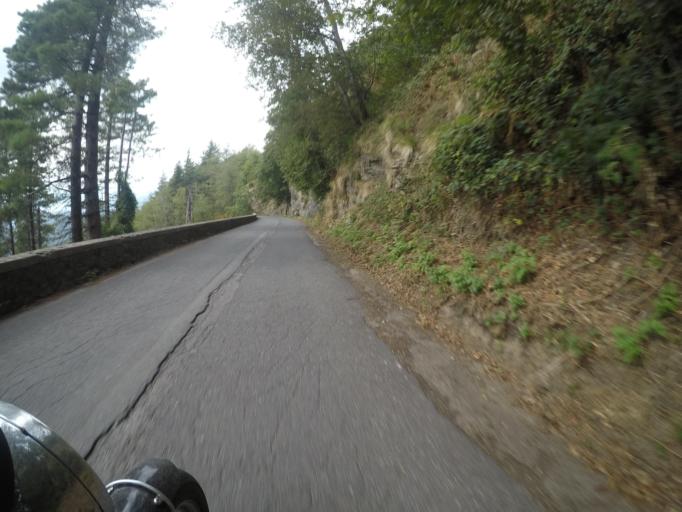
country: IT
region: Tuscany
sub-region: Provincia di Massa-Carrara
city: Carrara
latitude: 44.1143
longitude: 10.1188
